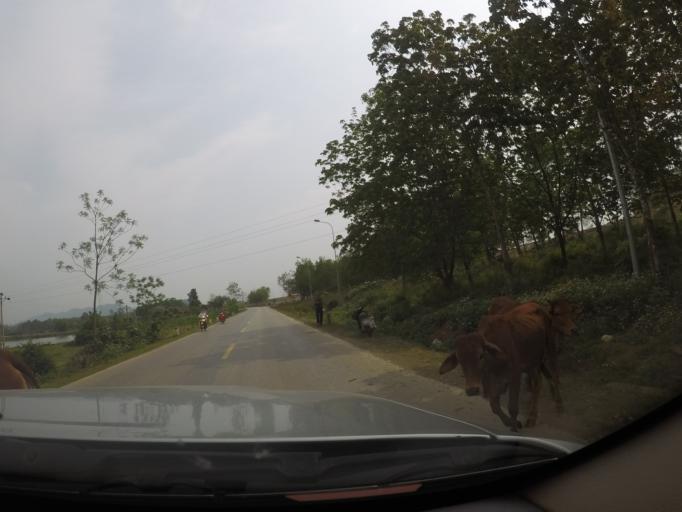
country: VN
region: Nghe An
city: Cau Giat
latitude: 19.3622
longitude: 105.4653
